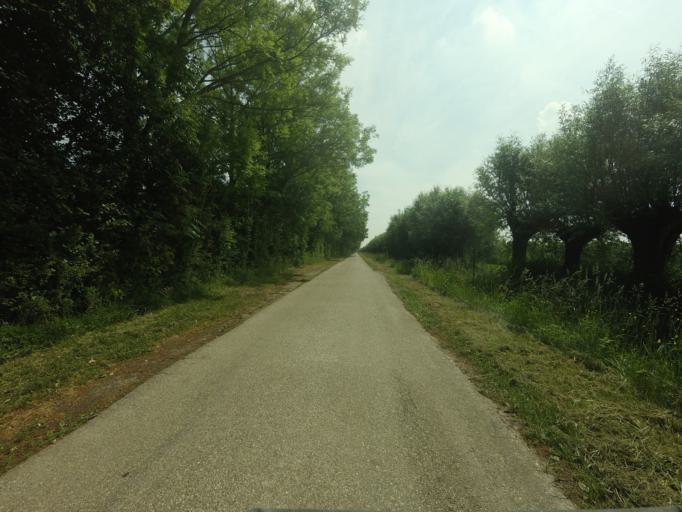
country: NL
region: Gelderland
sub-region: Gemeente Culemborg
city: Culemborg
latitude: 51.9942
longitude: 5.2250
